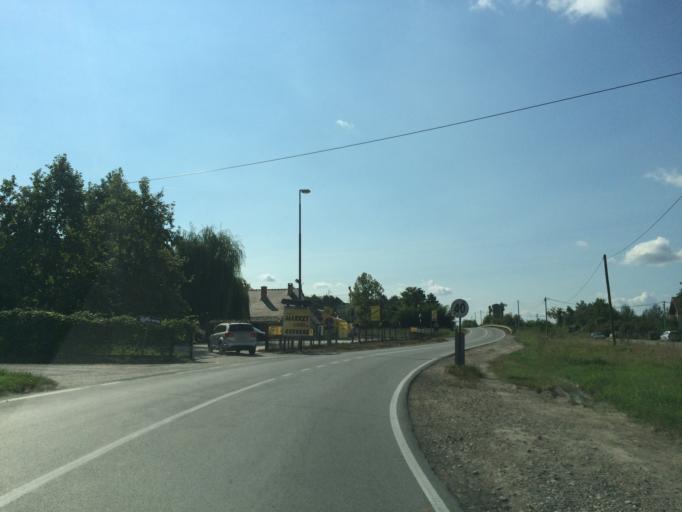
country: RS
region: Autonomna Pokrajina Vojvodina
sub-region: Juznobacki Okrug
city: Novi Sad
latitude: 45.2181
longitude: 19.8182
